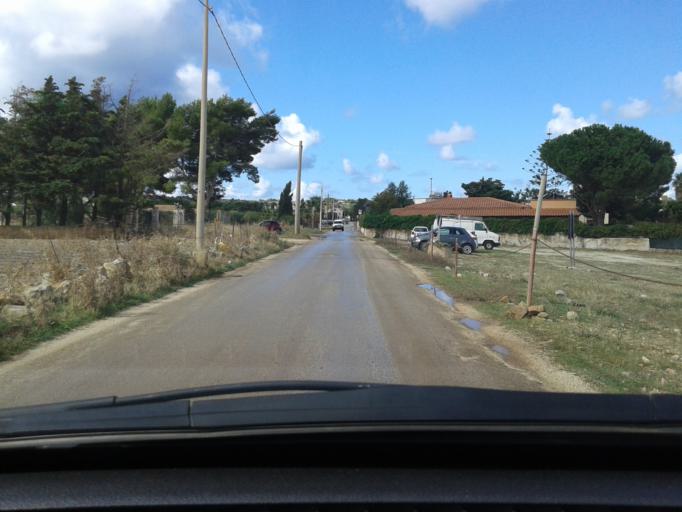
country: IT
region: Sicily
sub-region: Trapani
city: San Vito Lo Capo
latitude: 38.1688
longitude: 12.7431
